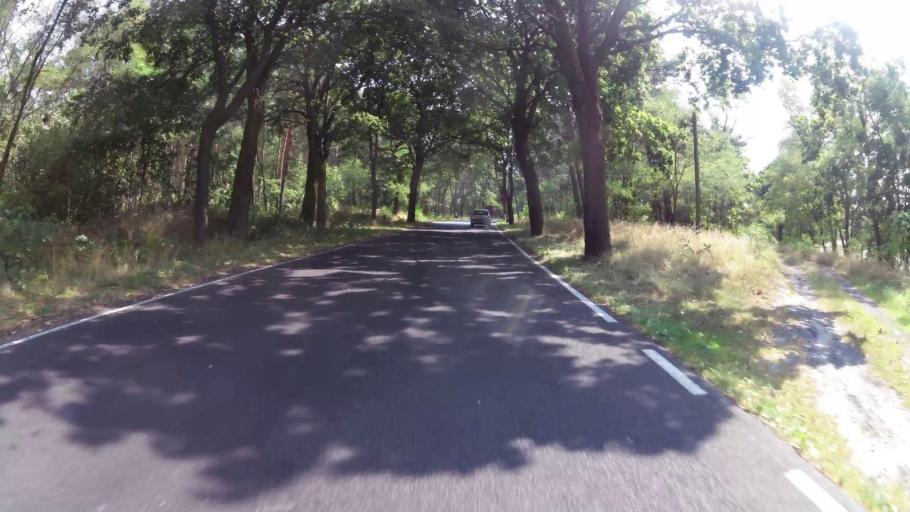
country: PL
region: West Pomeranian Voivodeship
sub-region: Powiat gryfinski
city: Moryn
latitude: 52.8379
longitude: 14.4078
